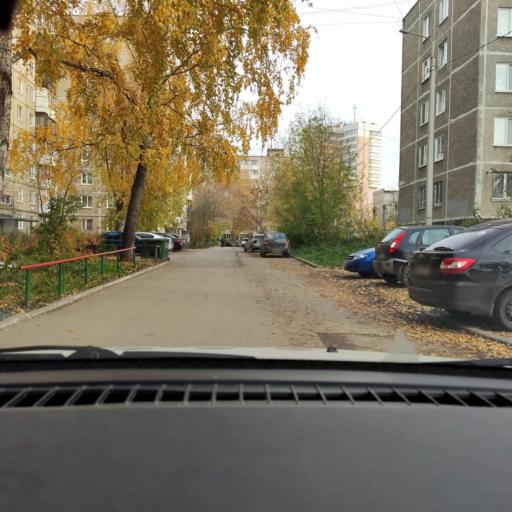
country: RU
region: Perm
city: Perm
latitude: 58.0616
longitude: 56.3526
